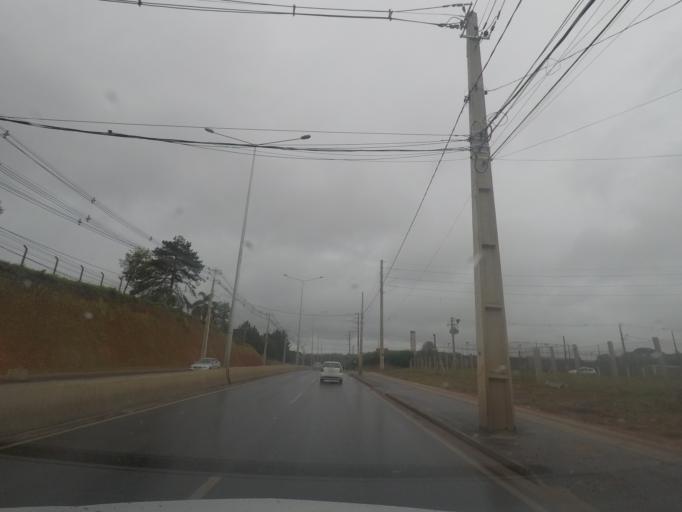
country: BR
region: Parana
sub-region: Piraquara
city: Piraquara
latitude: -25.4573
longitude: -49.0790
